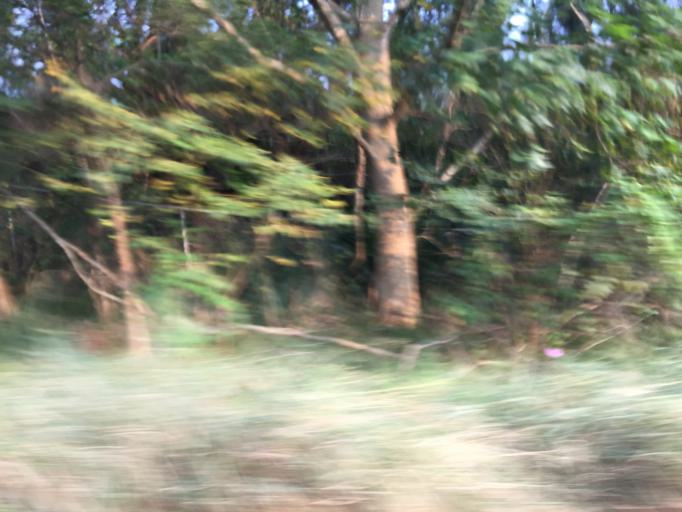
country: TW
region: Taiwan
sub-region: Hsinchu
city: Hsinchu
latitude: 24.7787
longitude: 120.9551
